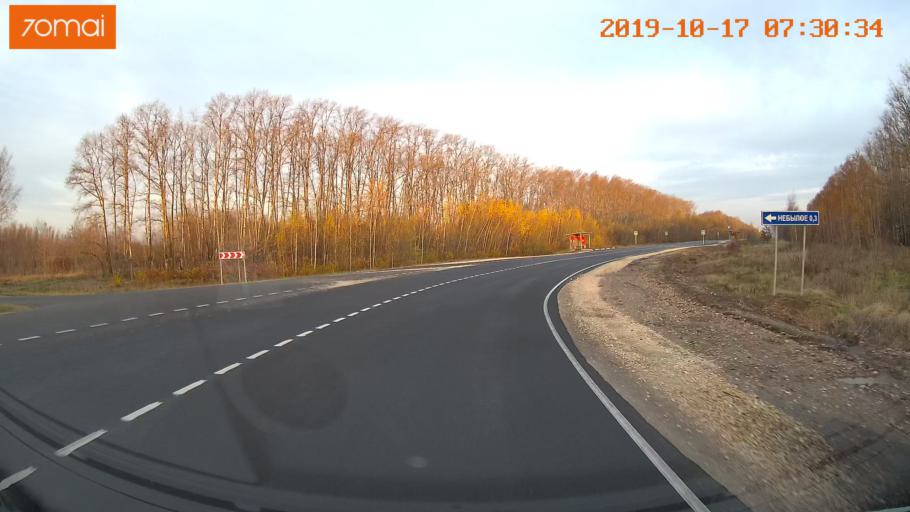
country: RU
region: Ivanovo
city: Gavrilov Posad
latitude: 56.3791
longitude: 40.0082
